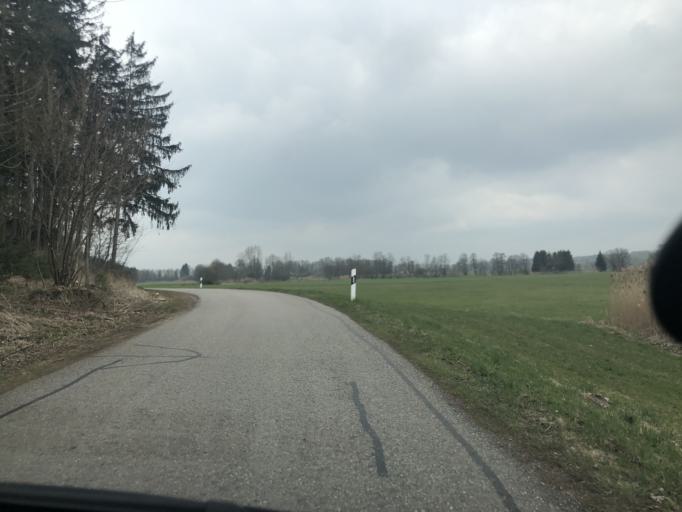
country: DE
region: Bavaria
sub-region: Upper Bavaria
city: Zolling
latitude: 48.4387
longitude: 11.7586
